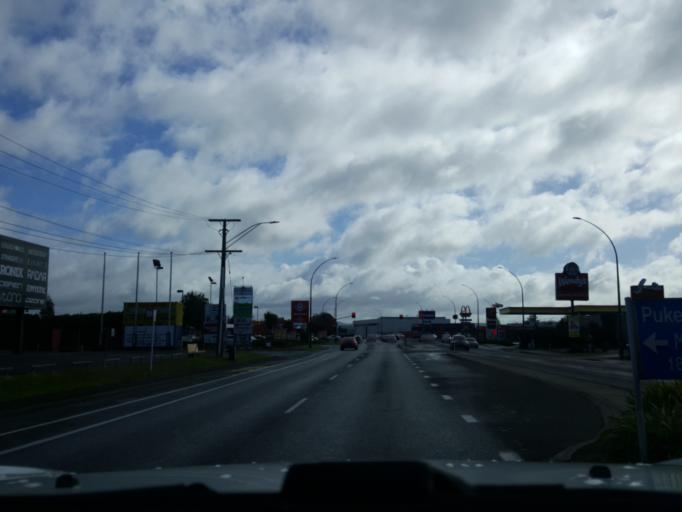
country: NZ
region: Waikato
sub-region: Hamilton City
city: Hamilton
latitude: -37.7535
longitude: 175.2417
